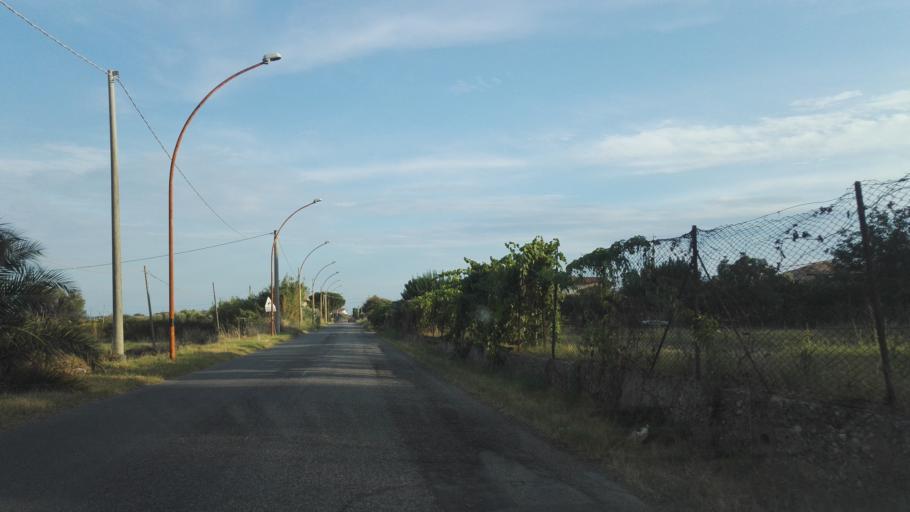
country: IT
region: Calabria
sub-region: Provincia di Reggio Calabria
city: Caulonia Marina
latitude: 38.3669
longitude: 16.4840
